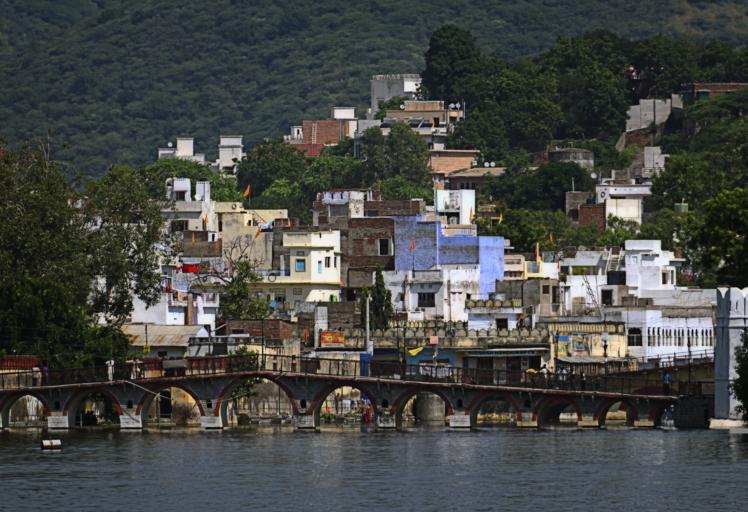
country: IN
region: Rajasthan
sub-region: Udaipur
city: Udaipur
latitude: 24.5730
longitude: 73.6829
